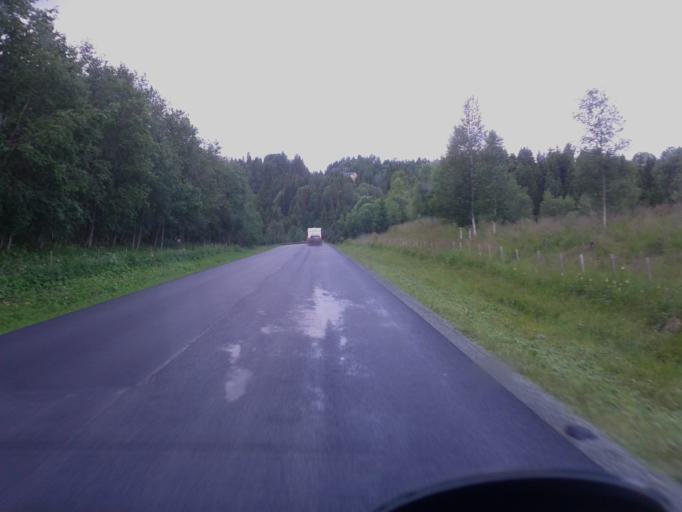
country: NO
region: Nord-Trondelag
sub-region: Grong
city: Grong
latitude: 64.5289
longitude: 12.3950
